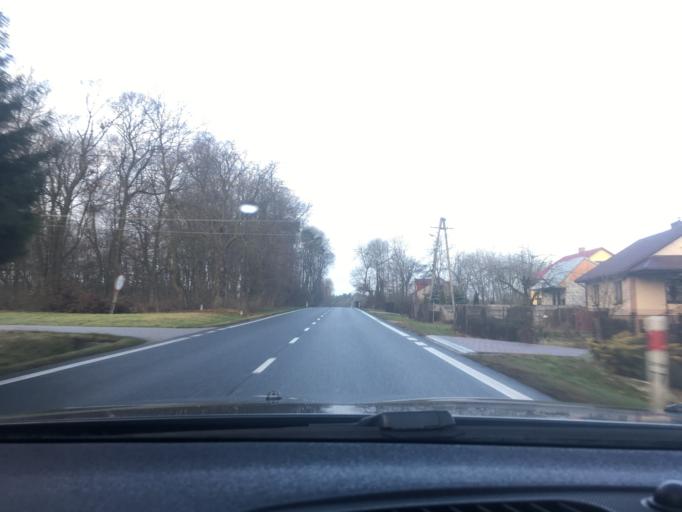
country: PL
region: Swietokrzyskie
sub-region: Powiat jedrzejowski
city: Imielno
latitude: 50.6227
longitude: 20.3967
